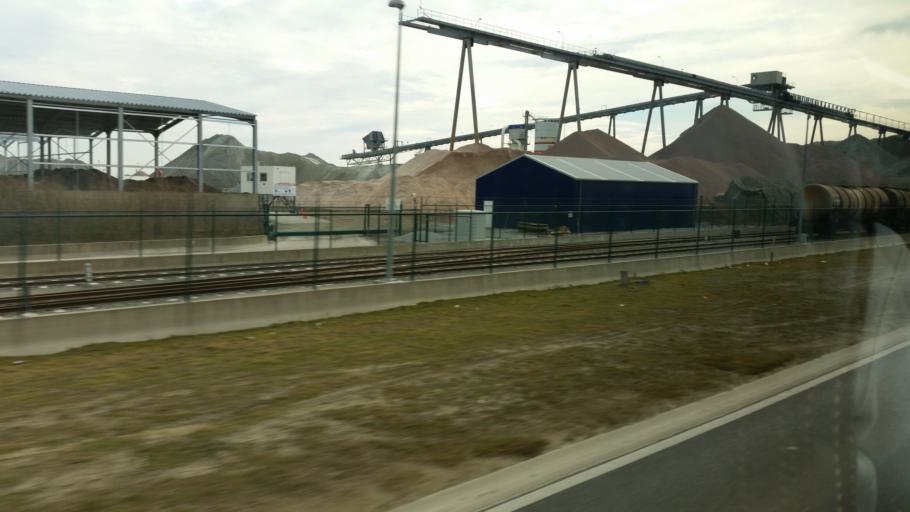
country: BE
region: Flanders
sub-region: Provincie Oost-Vlaanderen
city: Beveren
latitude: 51.2905
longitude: 4.2305
